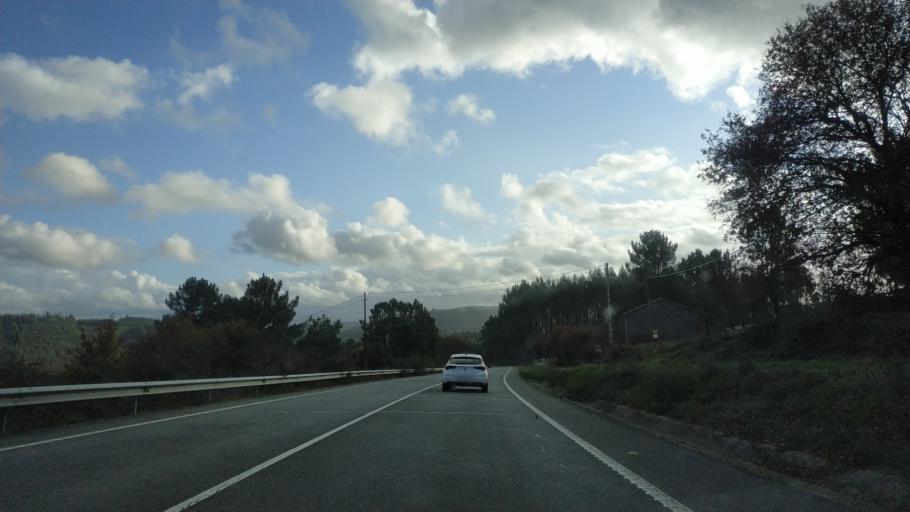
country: ES
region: Galicia
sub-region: Provincia da Coruna
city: Arzua
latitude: 42.9044
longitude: -8.1711
